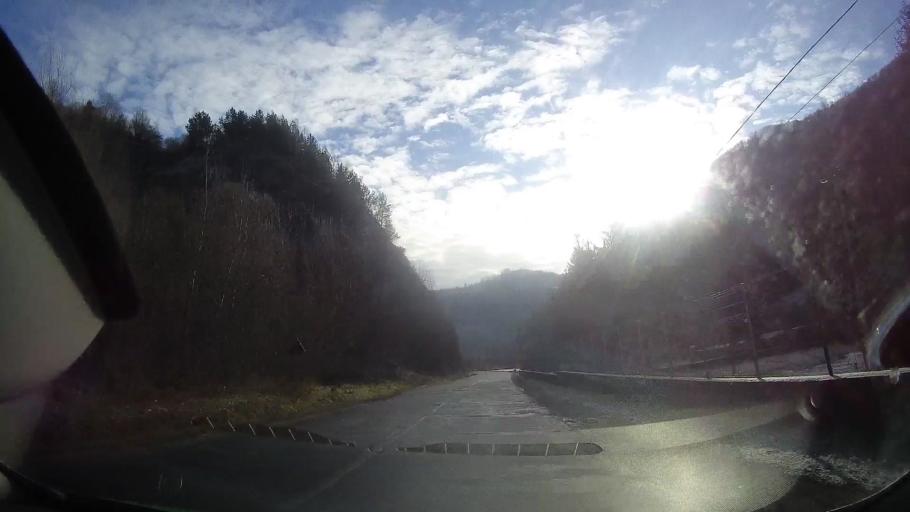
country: RO
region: Alba
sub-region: Comuna Sohodol
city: Sohodol
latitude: 46.3591
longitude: 23.0224
